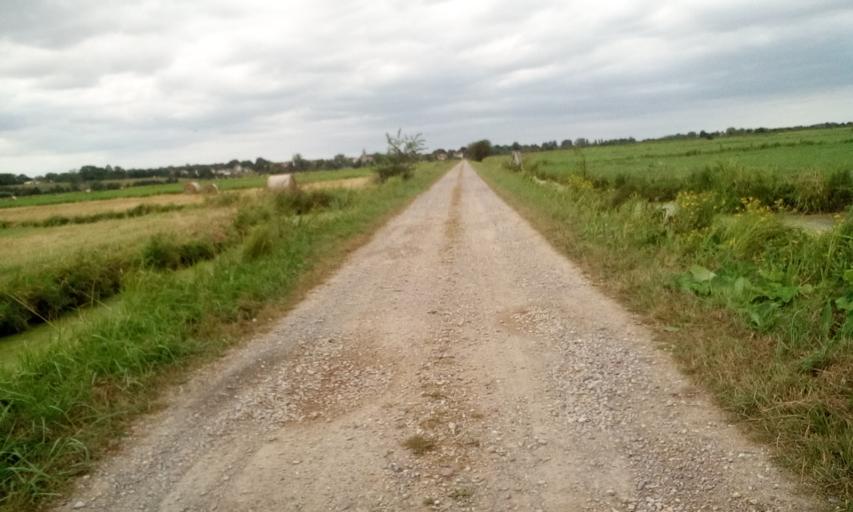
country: FR
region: Lower Normandy
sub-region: Departement du Calvados
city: Troarn
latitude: 49.1894
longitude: -0.1672
